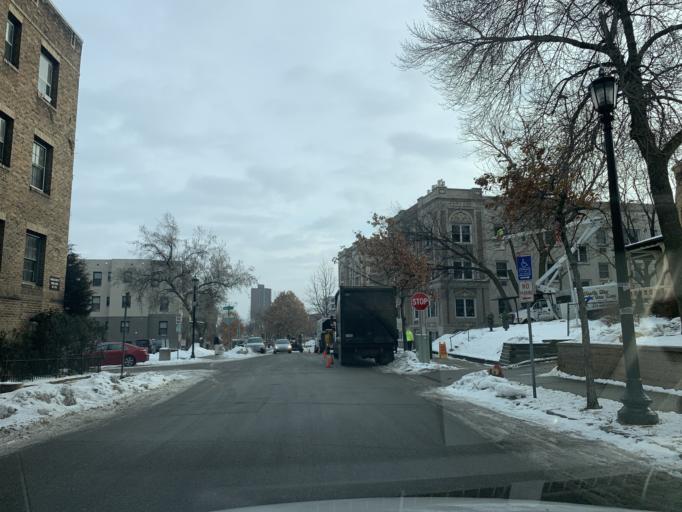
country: US
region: Minnesota
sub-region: Hennepin County
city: Minneapolis
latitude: 44.9665
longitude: -93.2813
